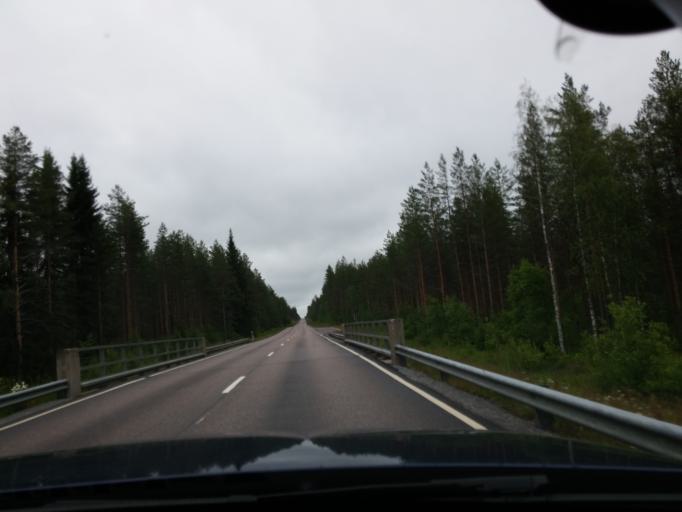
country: FI
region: Central Finland
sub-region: Saarijaervi-Viitasaari
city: Pylkoenmaeki
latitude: 62.5951
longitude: 24.6112
